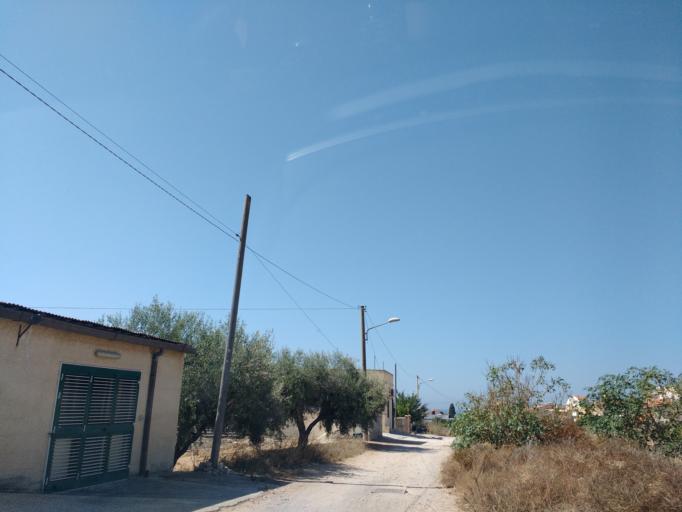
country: IT
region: Sicily
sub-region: Ragusa
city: Cava d'Aliga
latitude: 36.7325
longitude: 14.6859
